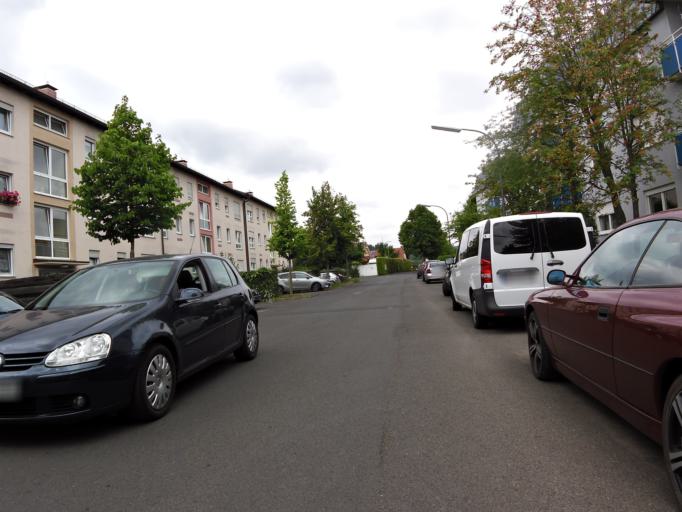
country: DE
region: Bavaria
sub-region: Regierungsbezirk Unterfranken
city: Wuerzburg
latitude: 49.7596
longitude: 9.9397
